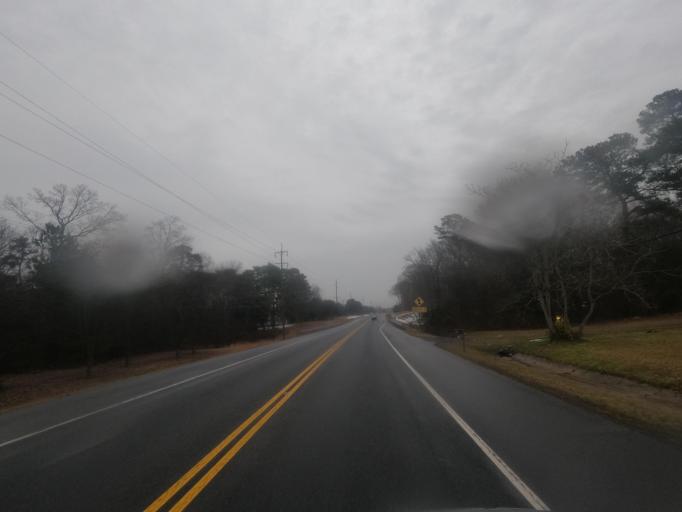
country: US
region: Maryland
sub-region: Dorchester County
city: Cambridge
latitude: 38.5691
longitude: -75.9874
